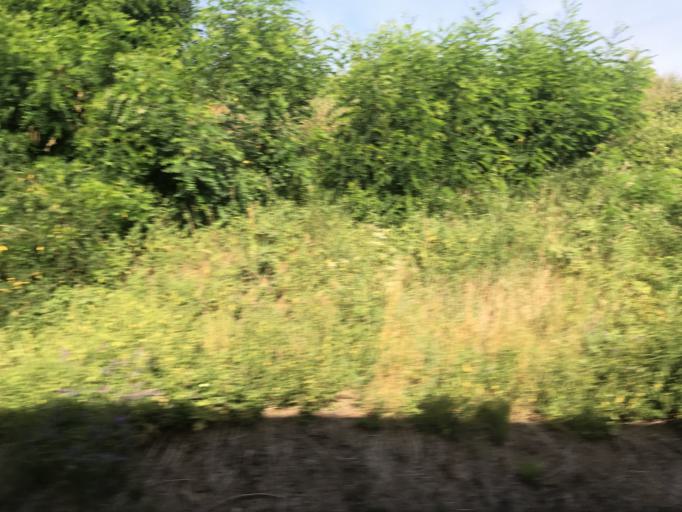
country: CZ
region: Jihocesky
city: Chotoviny
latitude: 49.5140
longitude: 14.6677
